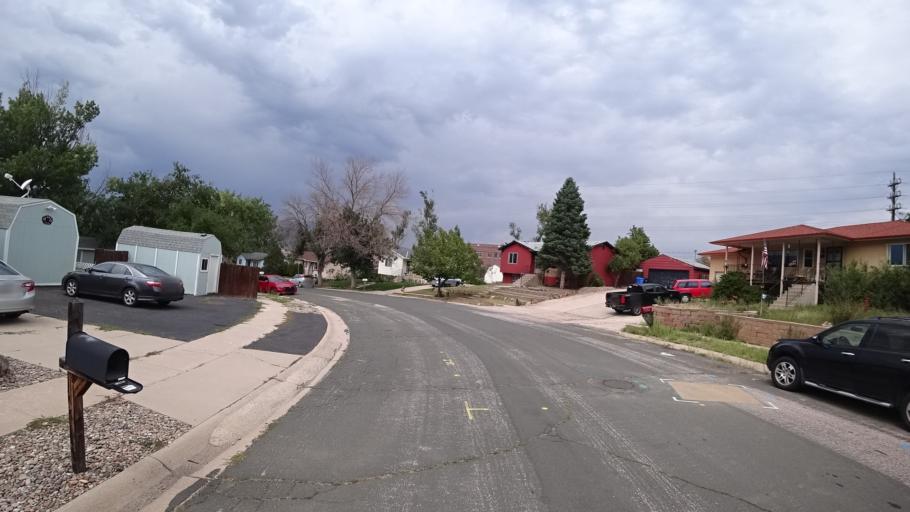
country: US
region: Colorado
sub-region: El Paso County
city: Colorado Springs
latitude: 38.8962
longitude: -104.8096
